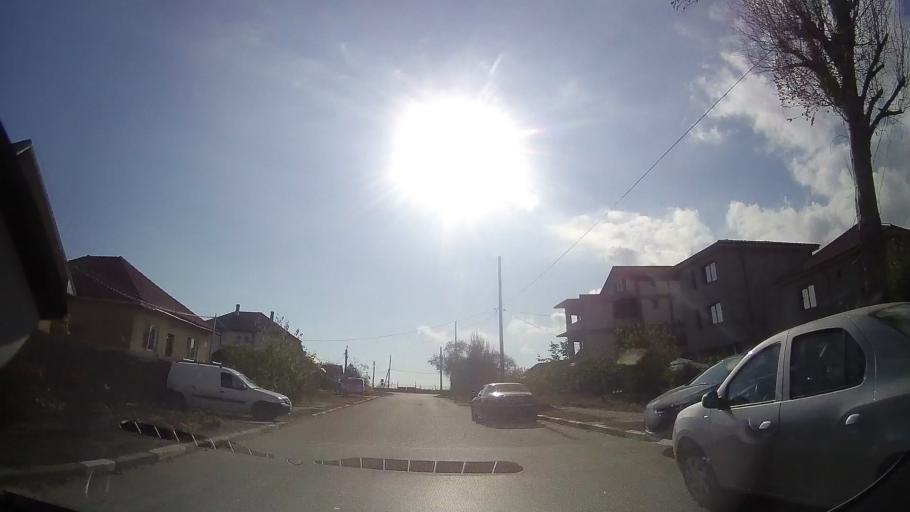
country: RO
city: Eforie Sud
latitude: 44.0152
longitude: 28.6474
